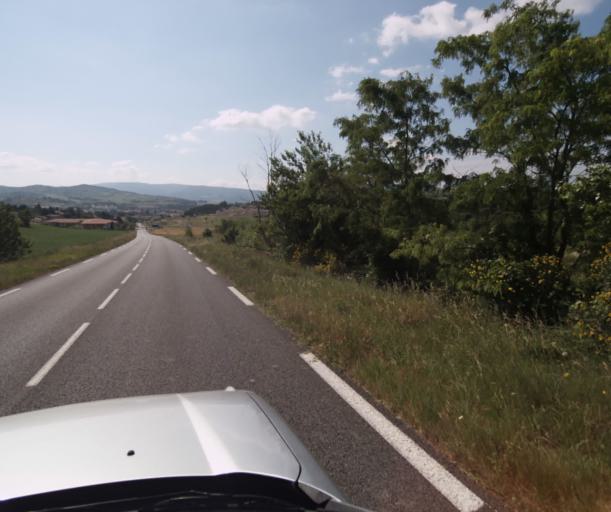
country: FR
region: Languedoc-Roussillon
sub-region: Departement de l'Aude
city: Limoux
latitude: 43.0712
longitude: 2.2020
